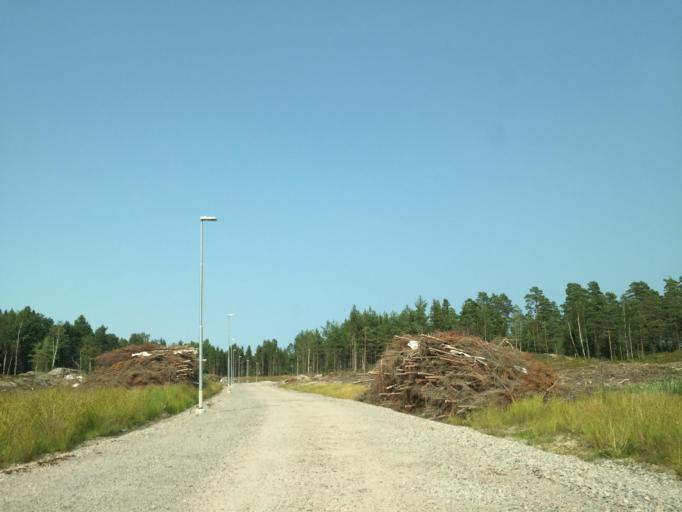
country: SE
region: Vaestra Goetaland
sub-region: Vanersborgs Kommun
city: Vanersborg
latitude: 58.3624
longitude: 12.2860
